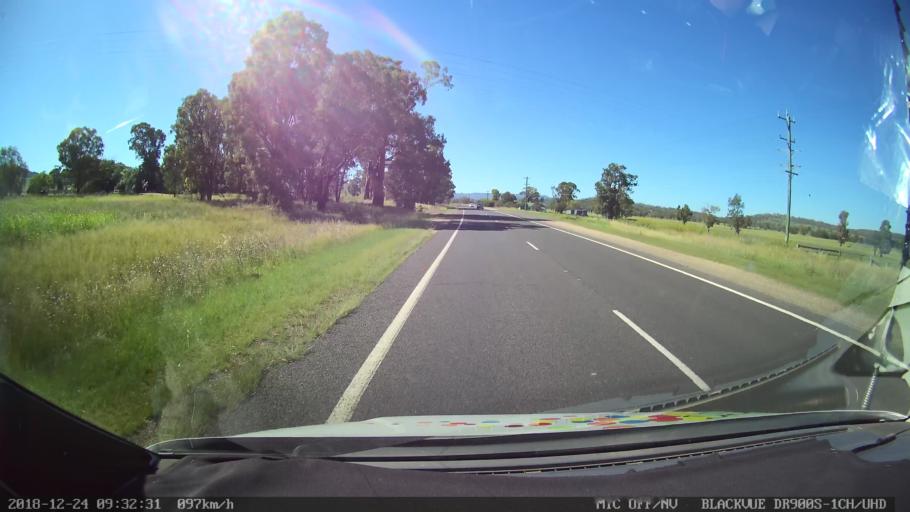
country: AU
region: New South Wales
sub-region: Liverpool Plains
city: Quirindi
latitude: -31.5916
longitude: 150.7032
